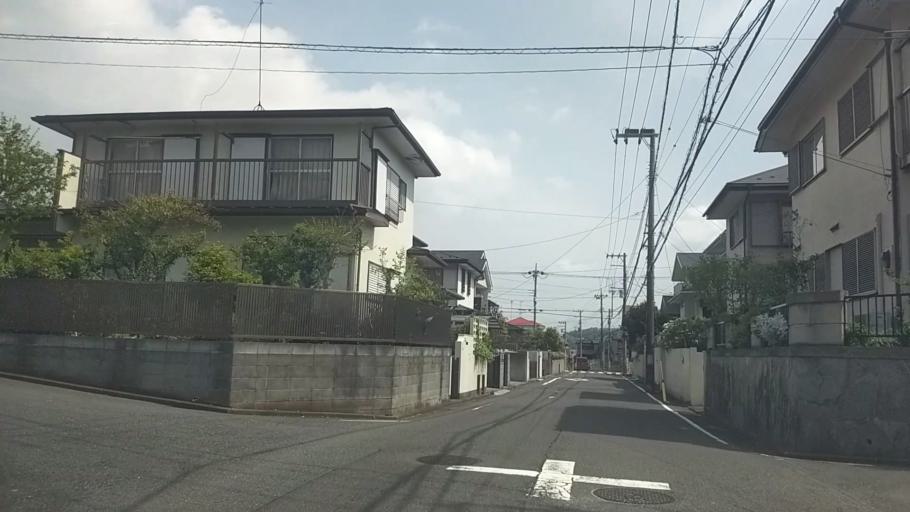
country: JP
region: Kanagawa
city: Yokohama
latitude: 35.3898
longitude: 139.5915
